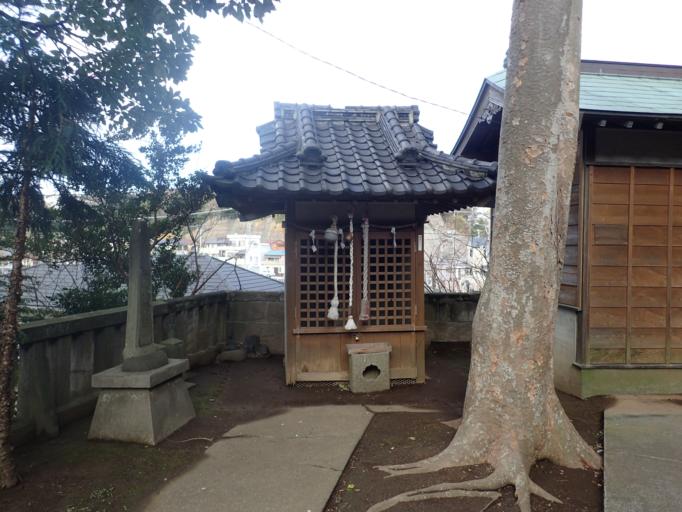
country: JP
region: Kanagawa
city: Miura
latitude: 35.1425
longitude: 139.6243
